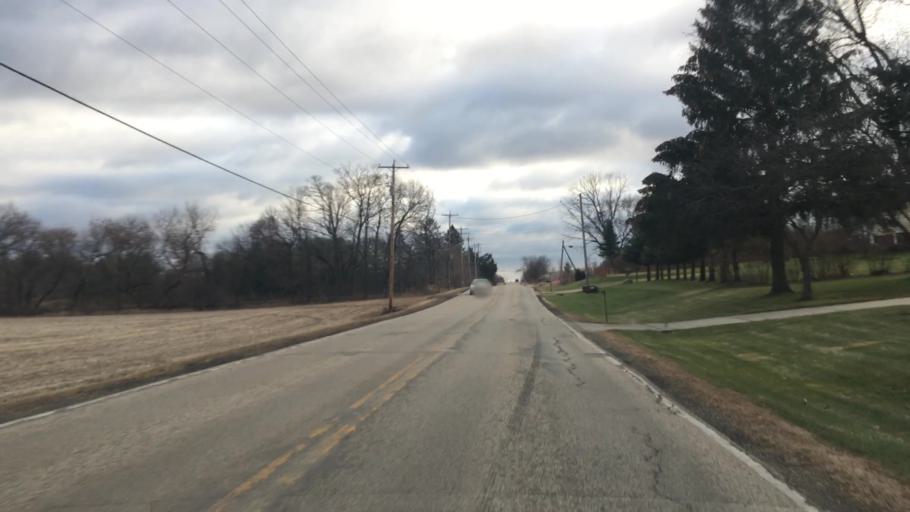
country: US
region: Wisconsin
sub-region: Washington County
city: Richfield
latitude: 43.2367
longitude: -88.2384
